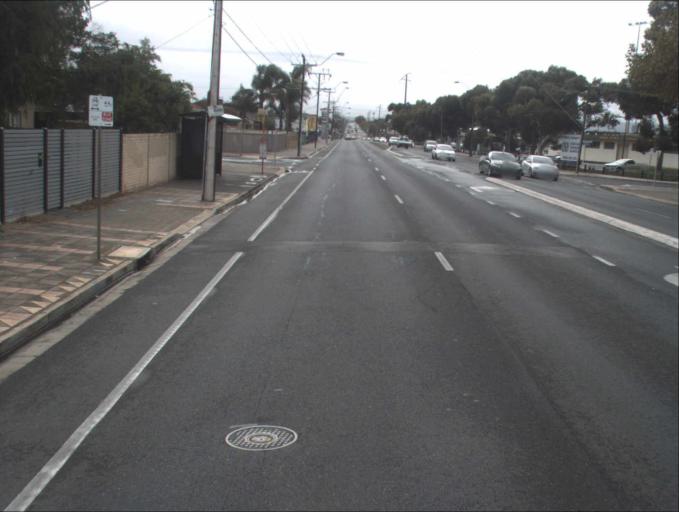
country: AU
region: South Australia
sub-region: Port Adelaide Enfield
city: Klemzig
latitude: -34.8769
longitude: 138.6295
